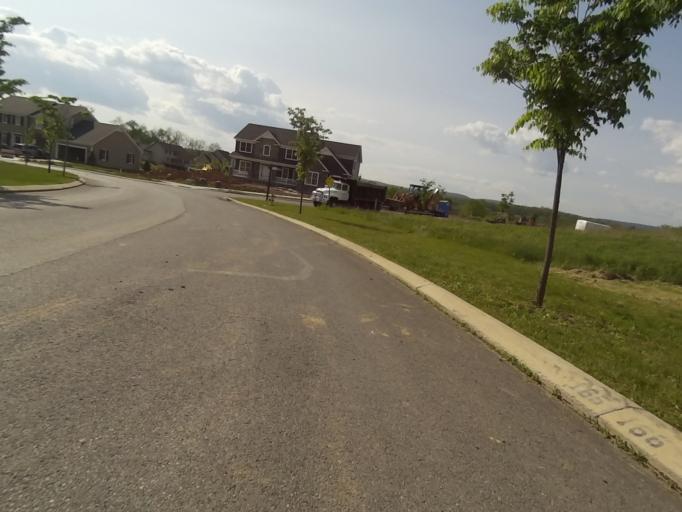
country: US
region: Pennsylvania
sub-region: Centre County
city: Houserville
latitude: 40.8296
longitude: -77.8217
